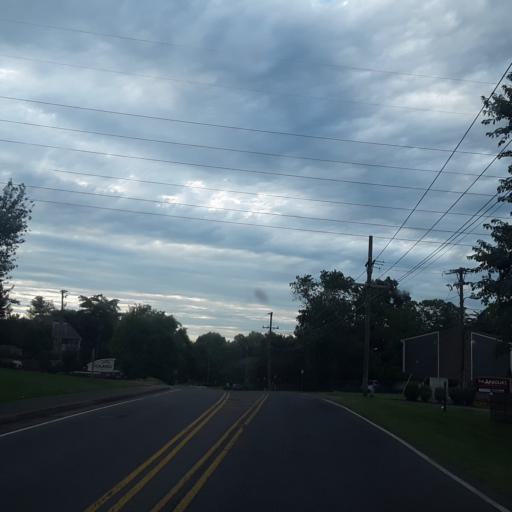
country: US
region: Tennessee
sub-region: Wilson County
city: Green Hill
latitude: 36.1635
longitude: -86.5974
